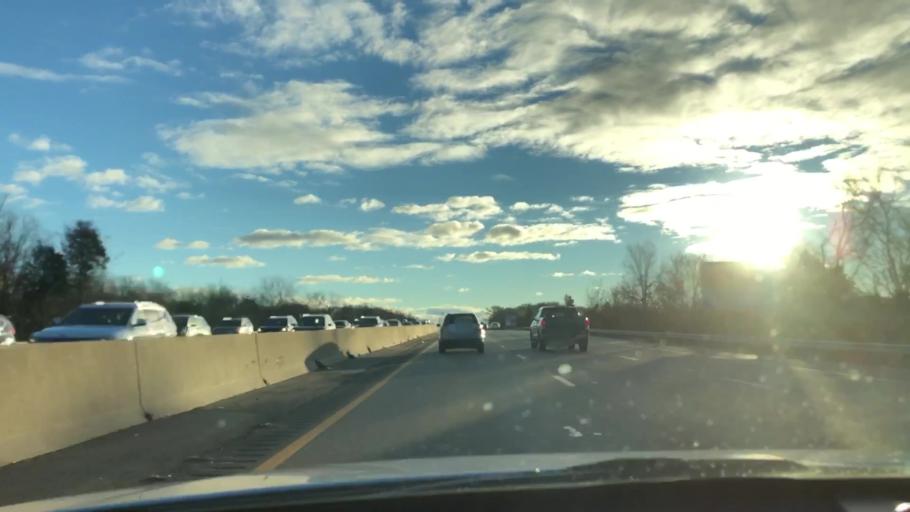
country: US
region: Massachusetts
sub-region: Norfolk County
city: Braintree
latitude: 42.2008
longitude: -70.9739
